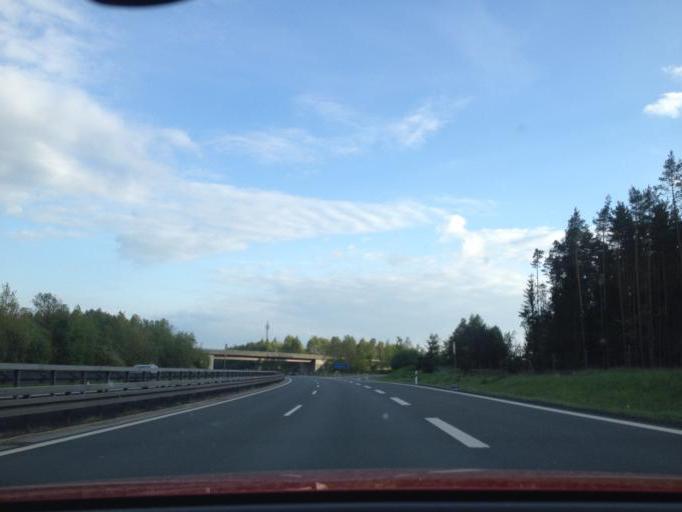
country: DE
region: Bavaria
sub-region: Upper Palatinate
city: Wiesau
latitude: 49.9143
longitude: 12.2198
